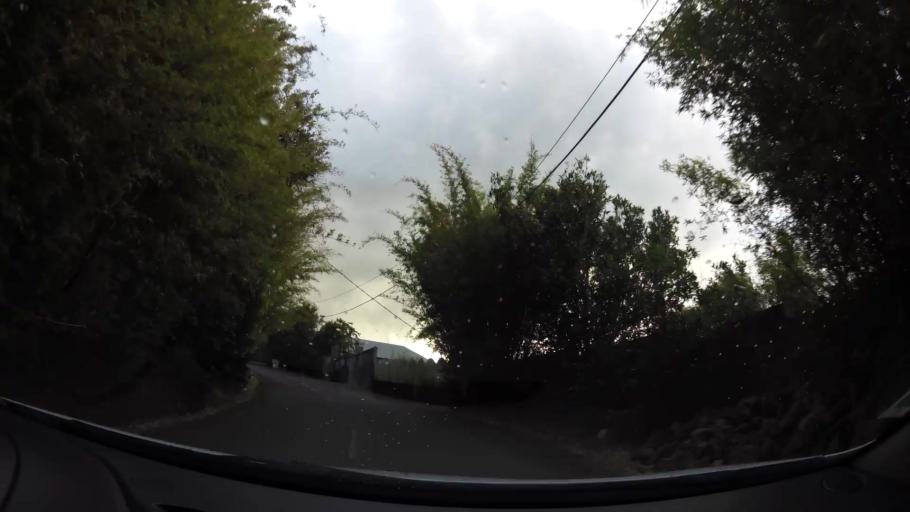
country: RE
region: Reunion
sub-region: Reunion
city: Saint-Denis
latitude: -20.9161
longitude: 55.4394
